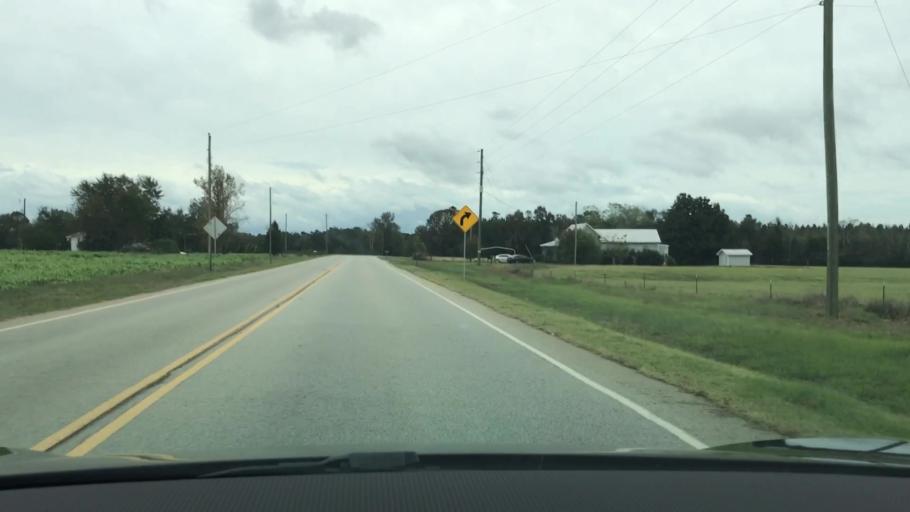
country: US
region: Georgia
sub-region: Jefferson County
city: Louisville
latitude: 33.0997
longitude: -82.4216
